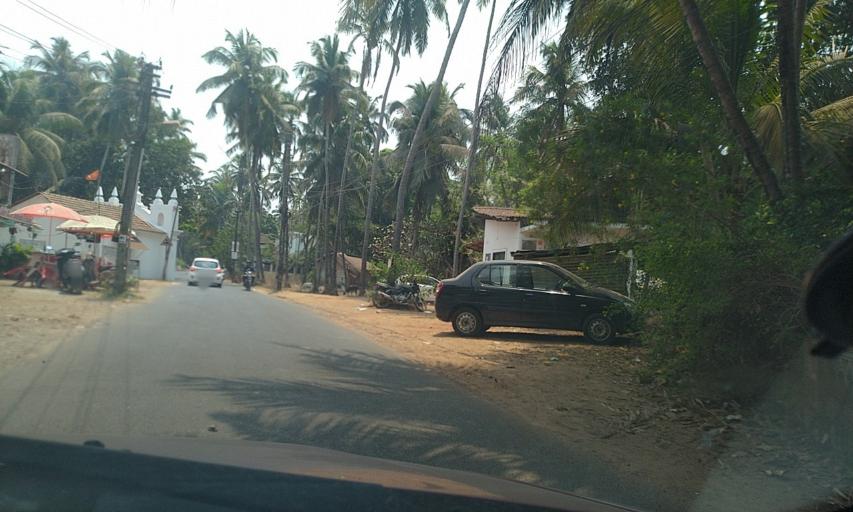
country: IN
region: Goa
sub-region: North Goa
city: Saligao
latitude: 15.5561
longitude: 73.7770
